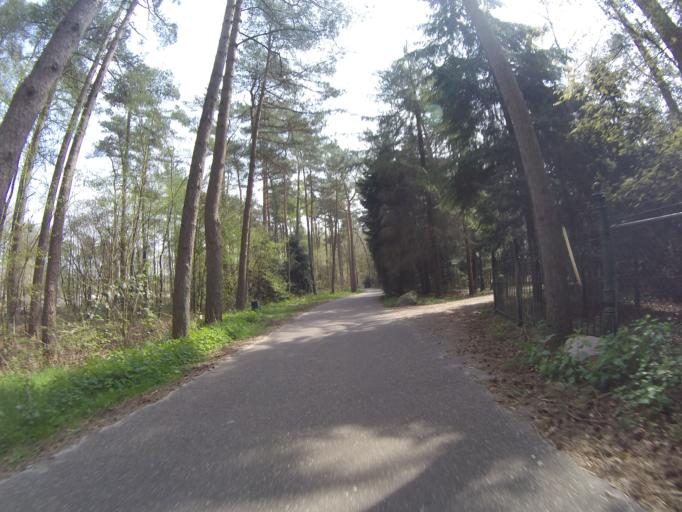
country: NL
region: Utrecht
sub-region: Gemeente Soest
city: Soest
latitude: 52.1425
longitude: 5.2875
